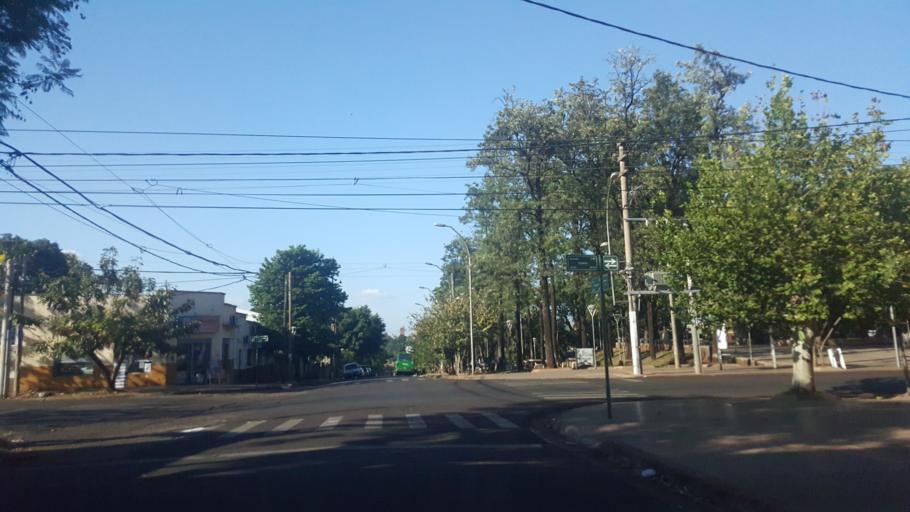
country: AR
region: Misiones
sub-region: Departamento de Capital
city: Posadas
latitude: -27.3852
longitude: -55.8944
